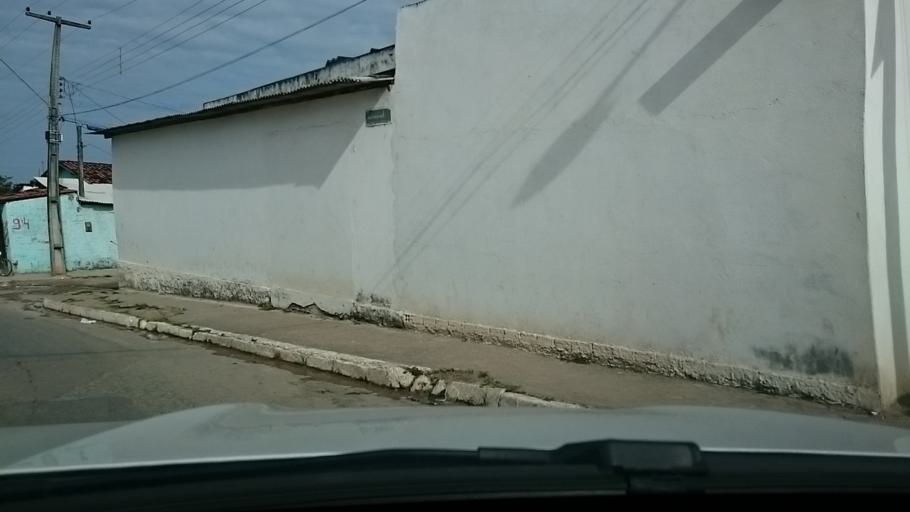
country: BR
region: Paraiba
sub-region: Joao Pessoa
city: Joao Pessoa
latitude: -7.1704
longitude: -34.8550
